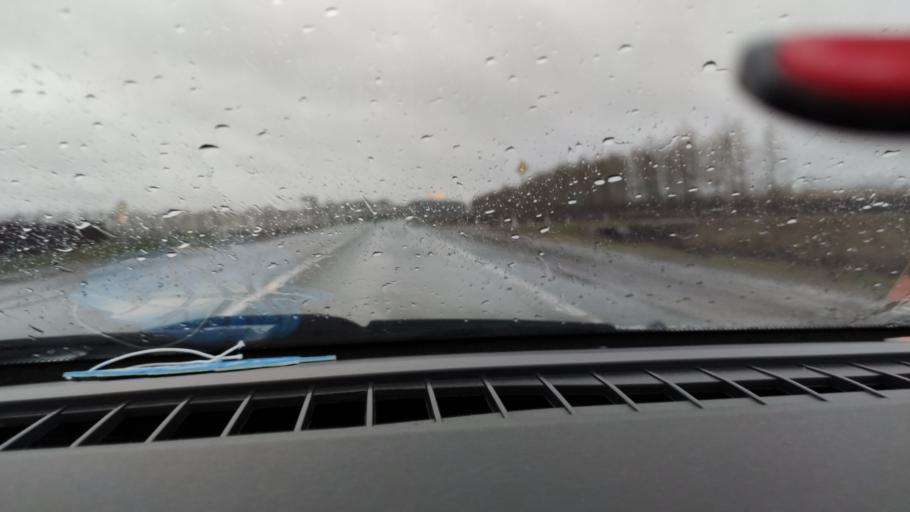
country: RU
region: Tatarstan
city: Mendeleyevsk
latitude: 55.8522
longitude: 52.2107
